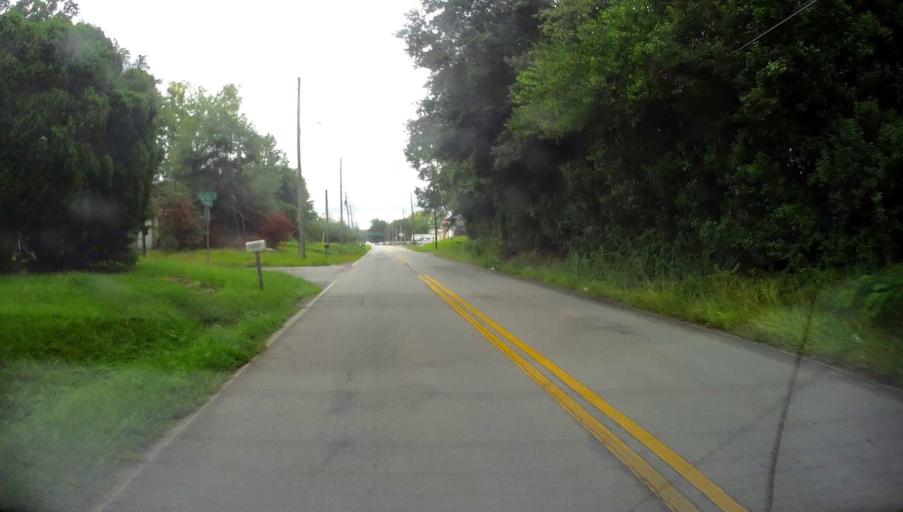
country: US
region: Georgia
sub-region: Bibb County
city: Macon
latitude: 32.7830
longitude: -83.6589
